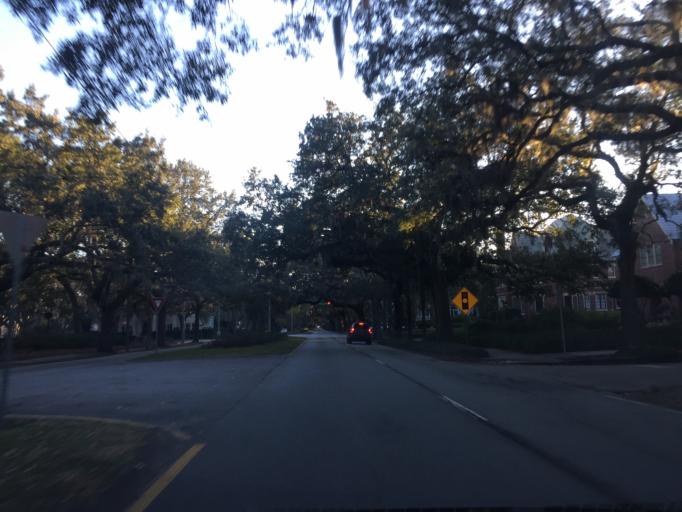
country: US
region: Georgia
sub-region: Chatham County
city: Savannah
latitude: 32.0499
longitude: -81.1004
